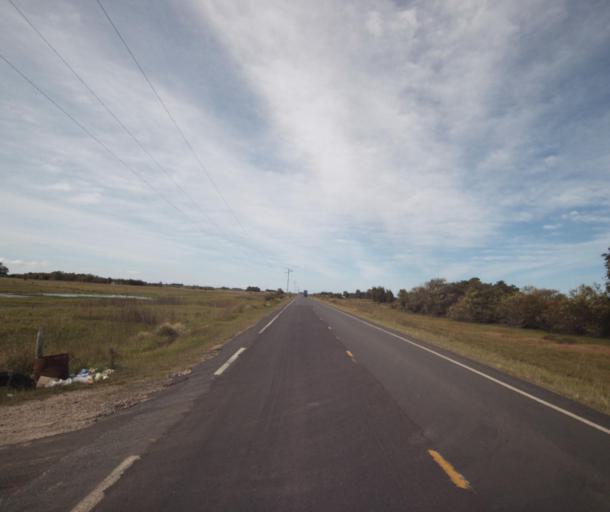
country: BR
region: Rio Grande do Sul
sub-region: Rio Grande
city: Rio Grande
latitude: -31.9454
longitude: -51.9769
